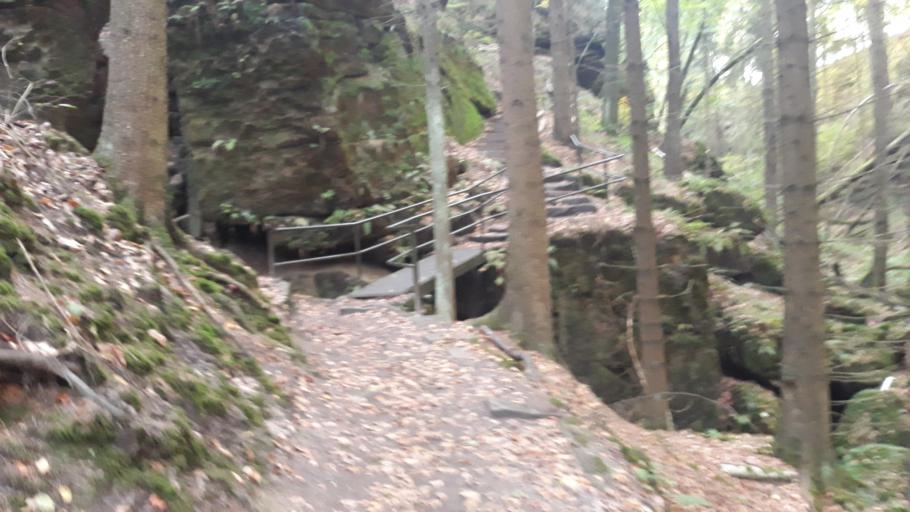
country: DE
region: Saxony
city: Stadt Wehlen
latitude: 50.9669
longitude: 14.0275
